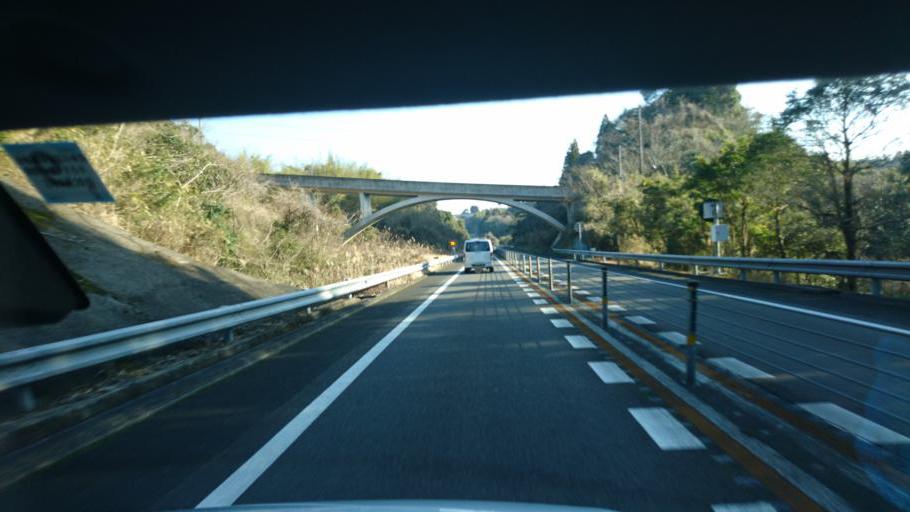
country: JP
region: Miyazaki
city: Tsuma
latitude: 32.0160
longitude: 131.3846
